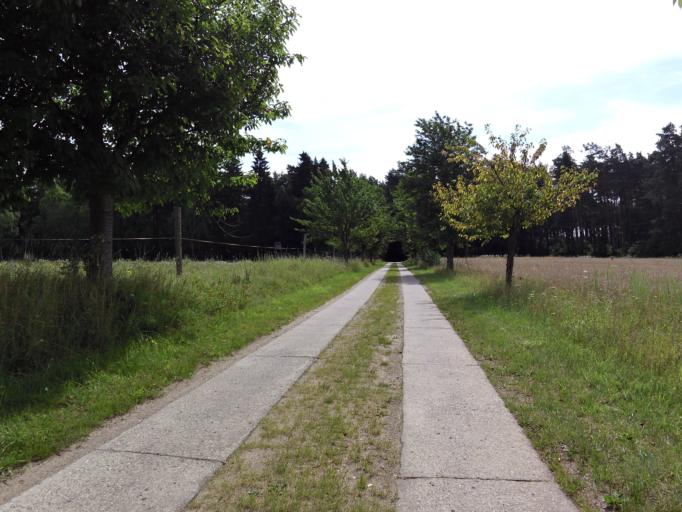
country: DE
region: Brandenburg
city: Lychen
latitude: 53.2829
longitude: 13.3620
